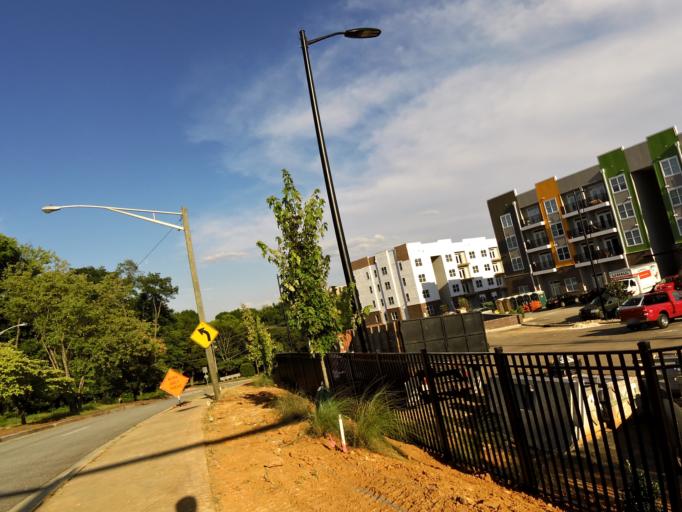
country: US
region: Tennessee
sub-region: Knox County
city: Knoxville
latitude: 35.9677
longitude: -83.9067
